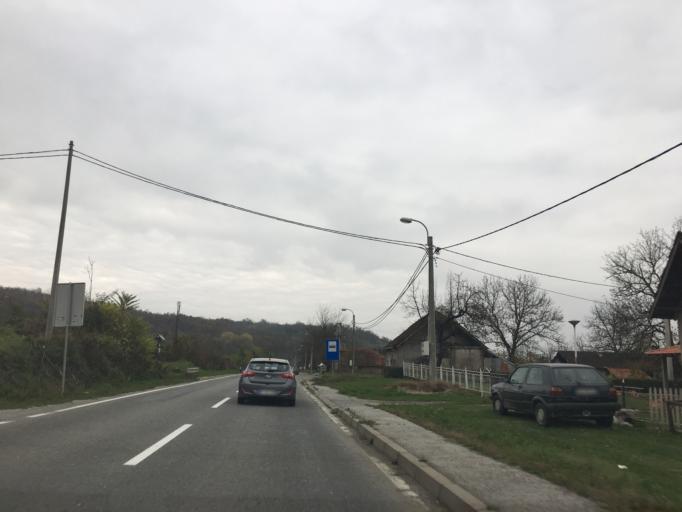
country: RS
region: Central Serbia
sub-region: Raski Okrug
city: Kraljevo
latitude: 43.7194
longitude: 20.7772
